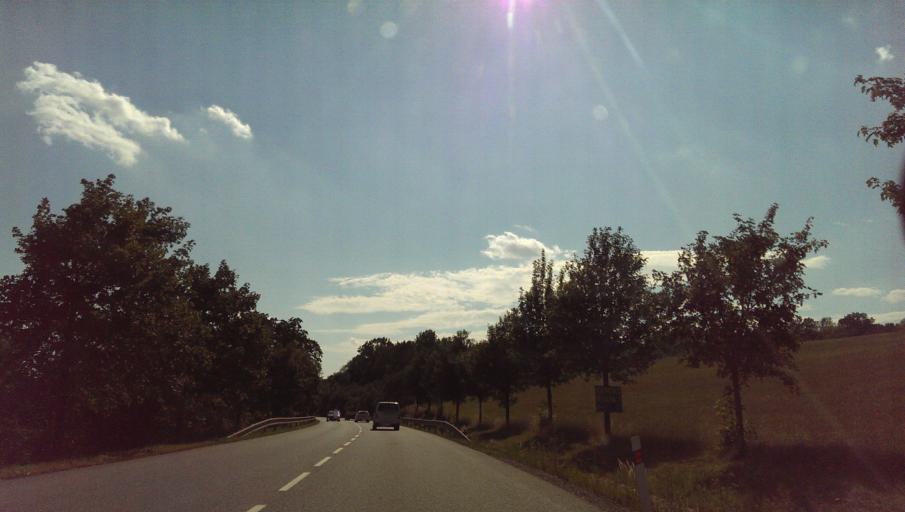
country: CZ
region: Zlin
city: Prusinovice
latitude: 49.3617
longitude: 17.6182
